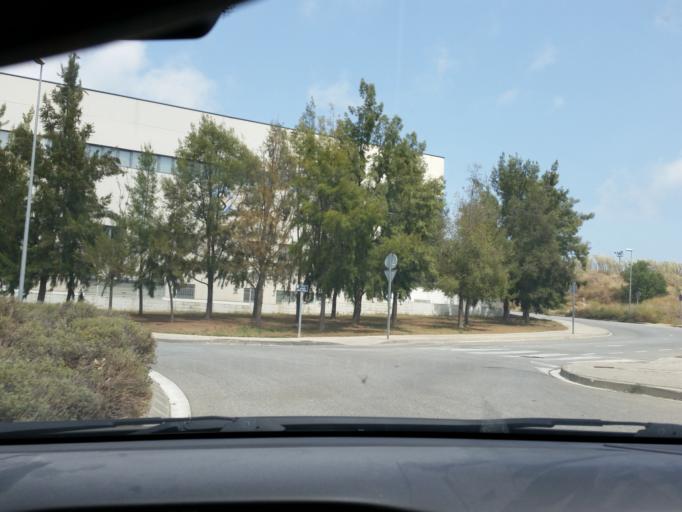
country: ES
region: Catalonia
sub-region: Provincia de Barcelona
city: Cabrils
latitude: 41.5142
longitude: 2.3693
